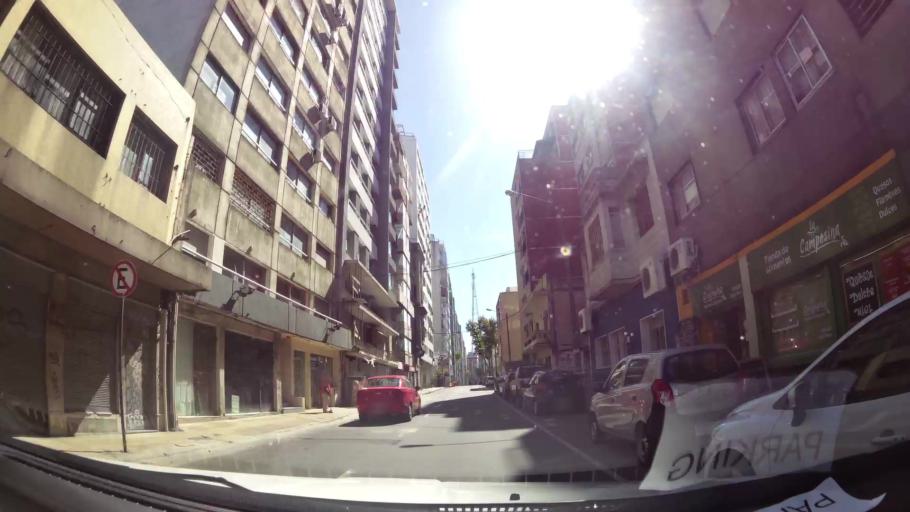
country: UY
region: Montevideo
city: Montevideo
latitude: -34.9009
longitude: -56.1723
